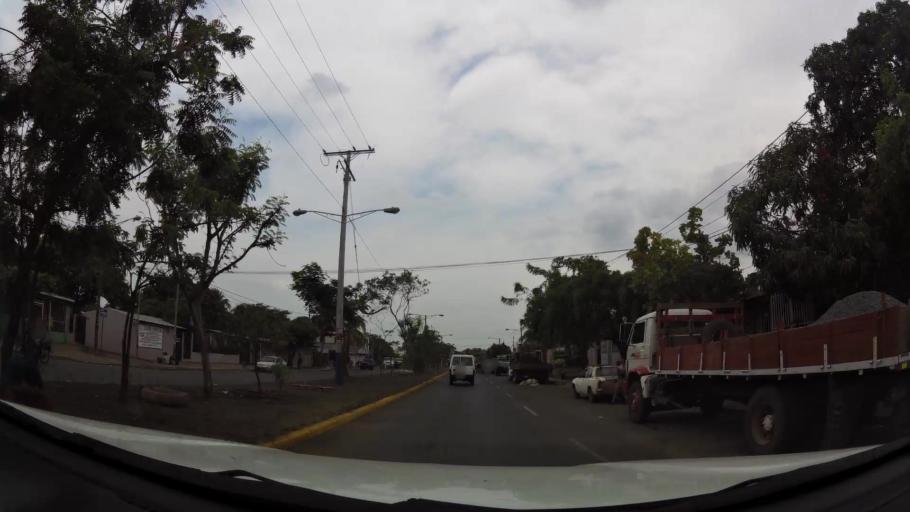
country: NI
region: Managua
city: Managua
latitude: 12.1266
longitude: -86.2176
